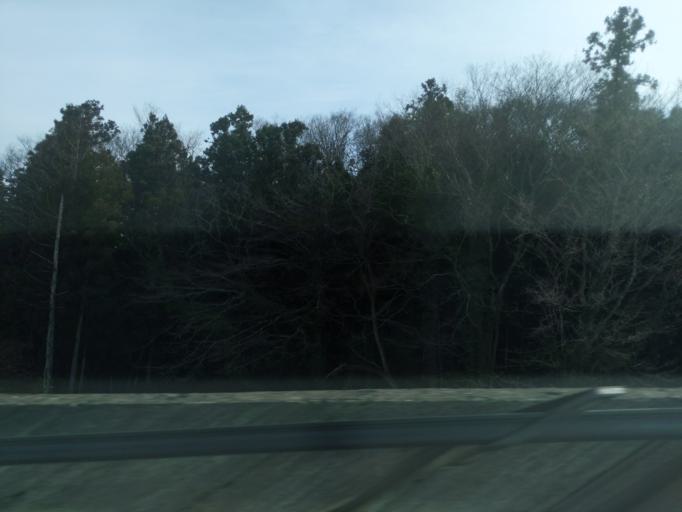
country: JP
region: Miyagi
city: Furukawa
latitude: 38.6229
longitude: 140.9987
